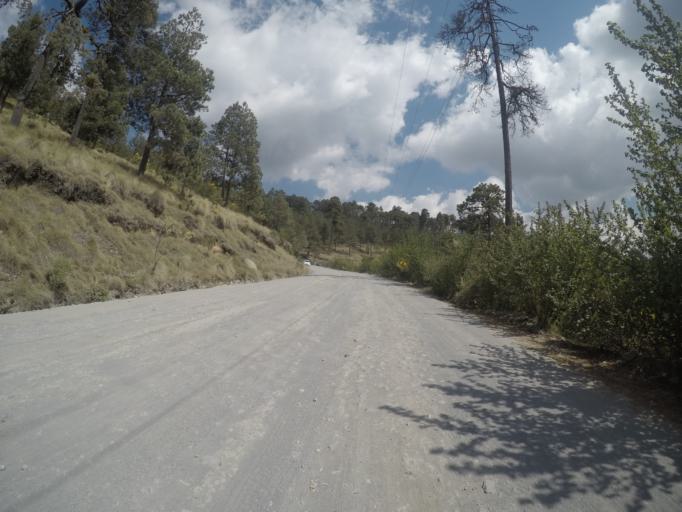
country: MX
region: Mexico
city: Cerro La Calera
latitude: 19.1403
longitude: -99.8006
